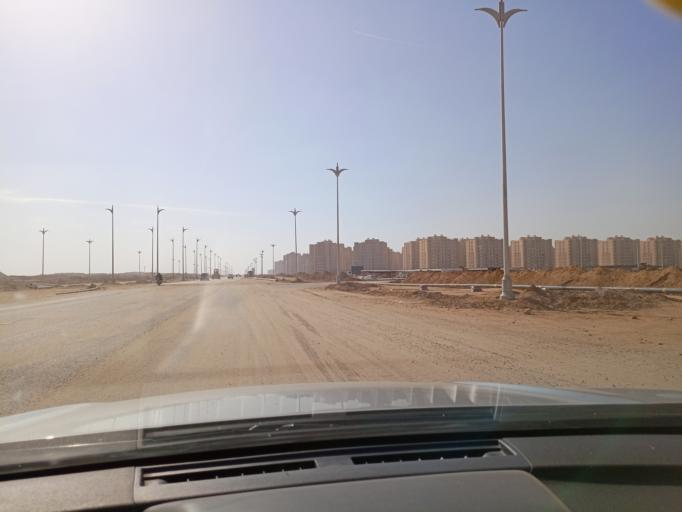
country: EG
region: Muhafazat al Qalyubiyah
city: Al Khankah
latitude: 30.0232
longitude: 31.6661
